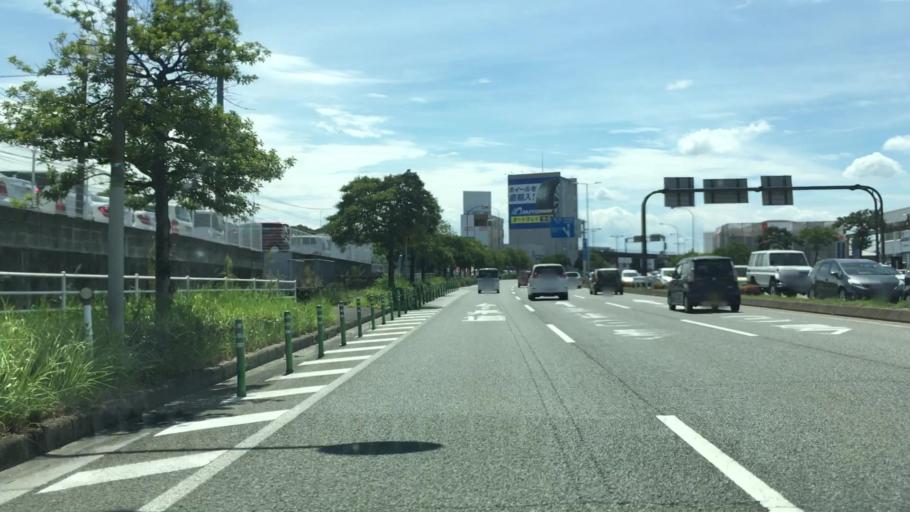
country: JP
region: Fukuoka
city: Onojo
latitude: 33.5286
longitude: 130.4941
